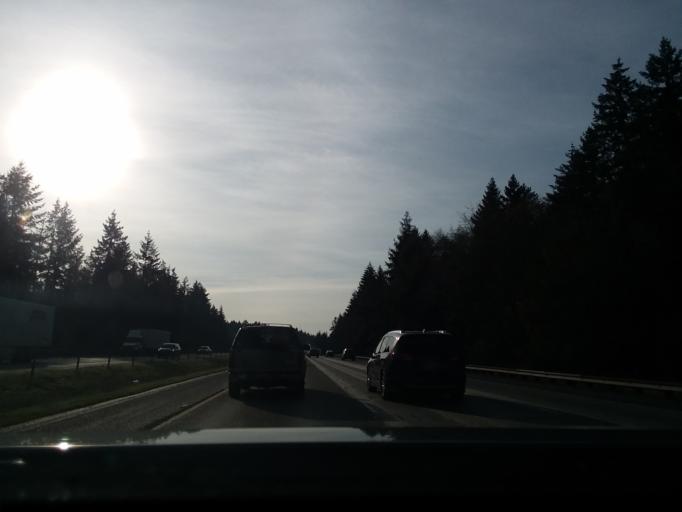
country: US
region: Washington
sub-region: Thurston County
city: Lacey
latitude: 47.0529
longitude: -122.8131
